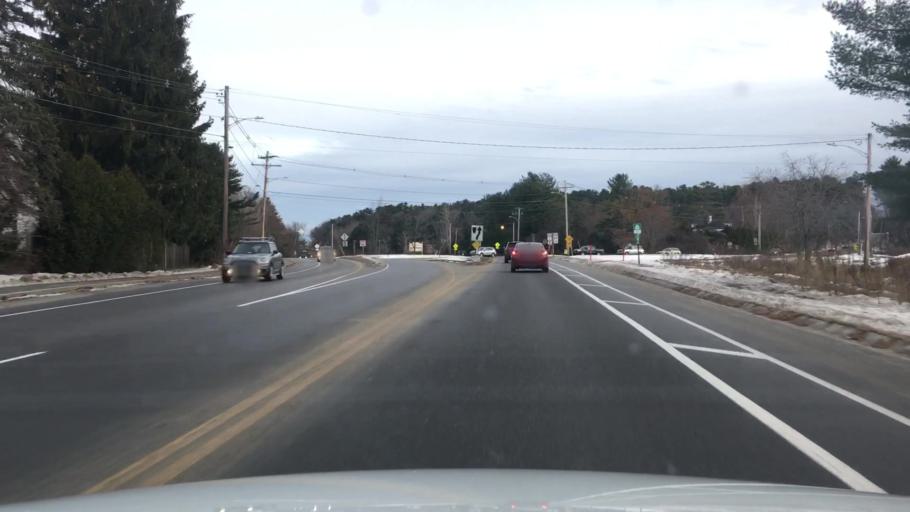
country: US
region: Maine
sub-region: Cumberland County
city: Falmouth
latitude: 43.7086
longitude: -70.2352
